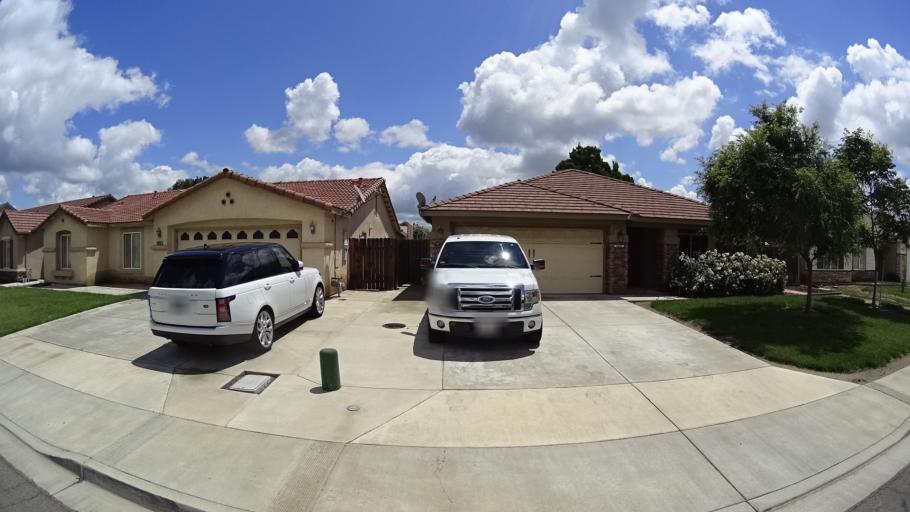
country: US
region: California
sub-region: Kings County
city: Lucerne
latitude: 36.3563
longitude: -119.6603
